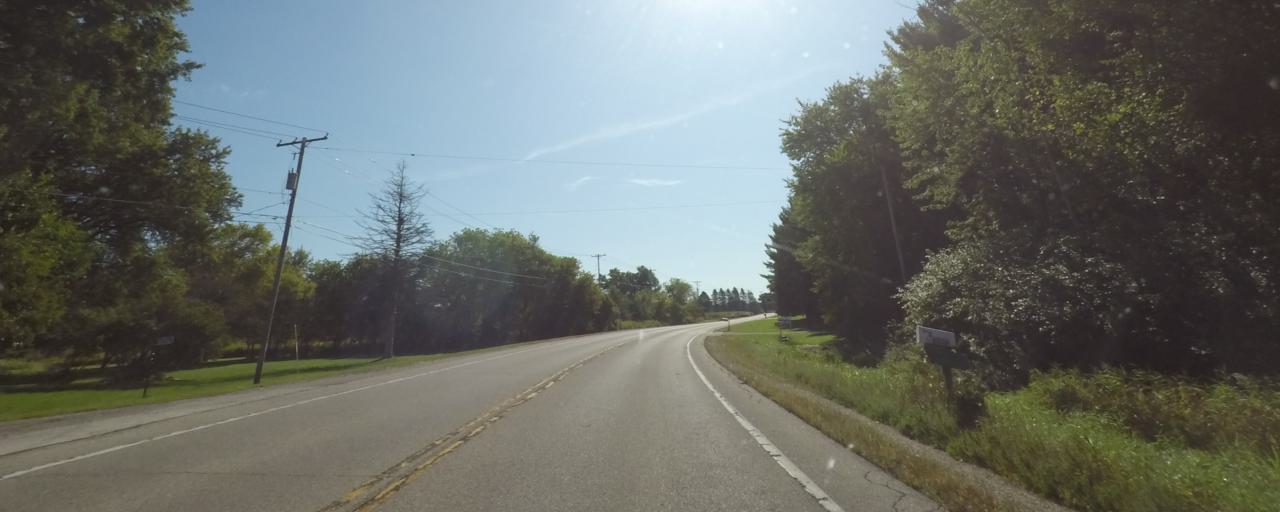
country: US
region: Wisconsin
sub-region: Waukesha County
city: Dousman
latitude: 43.0281
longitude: -88.5094
